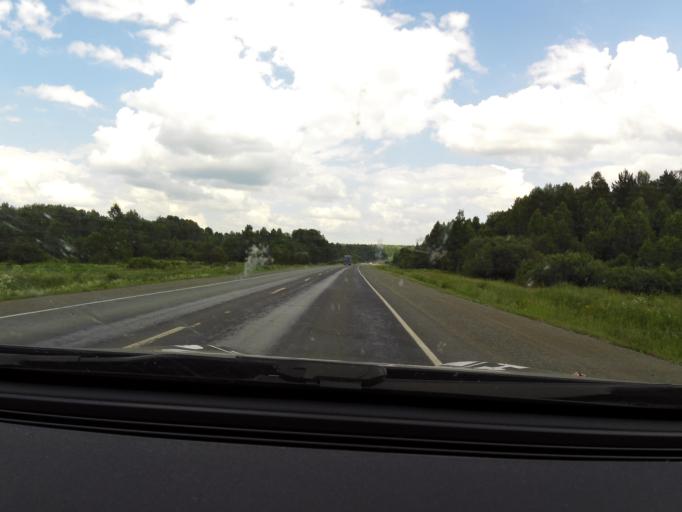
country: RU
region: Sverdlovsk
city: Bisert'
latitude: 56.8351
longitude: 58.9161
